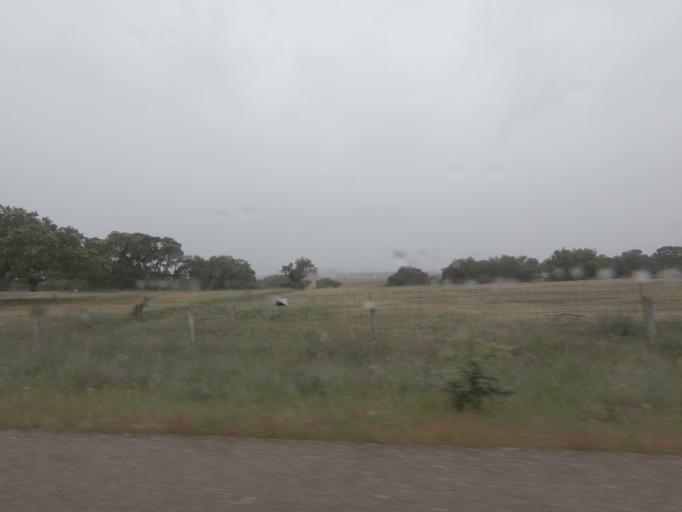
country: ES
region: Extremadura
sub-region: Provincia de Badajoz
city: Badajoz
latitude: 38.9496
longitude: -6.9130
